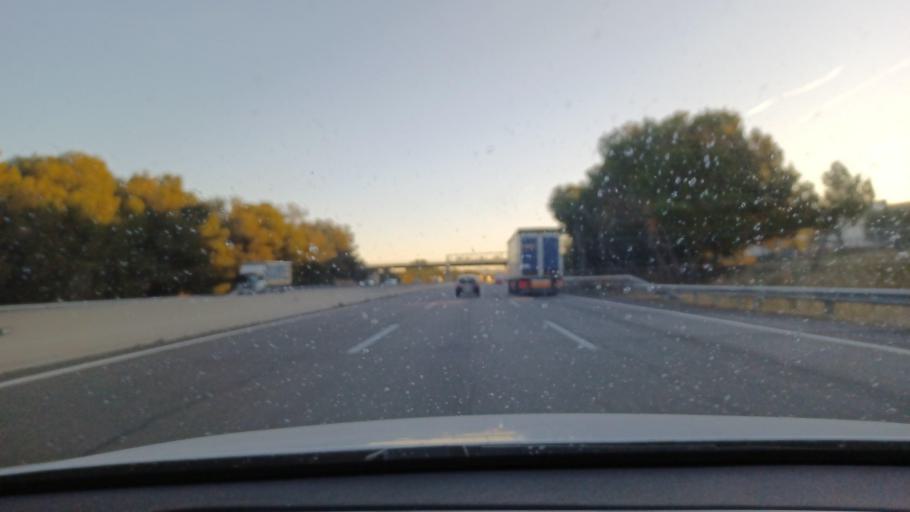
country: ES
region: Catalonia
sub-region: Provincia de Barcelona
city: Vilafranca del Penedes
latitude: 41.3277
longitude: 1.6532
